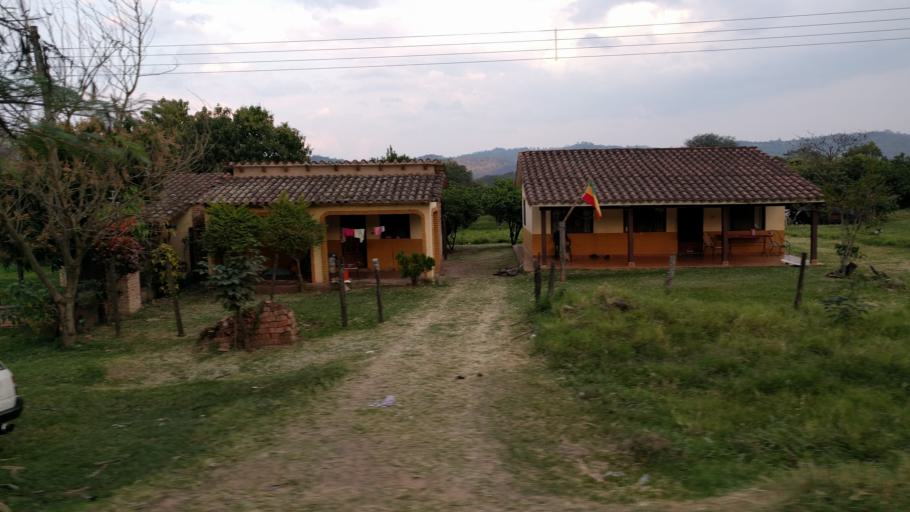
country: BO
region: Santa Cruz
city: Jorochito
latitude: -18.1303
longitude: -63.4695
